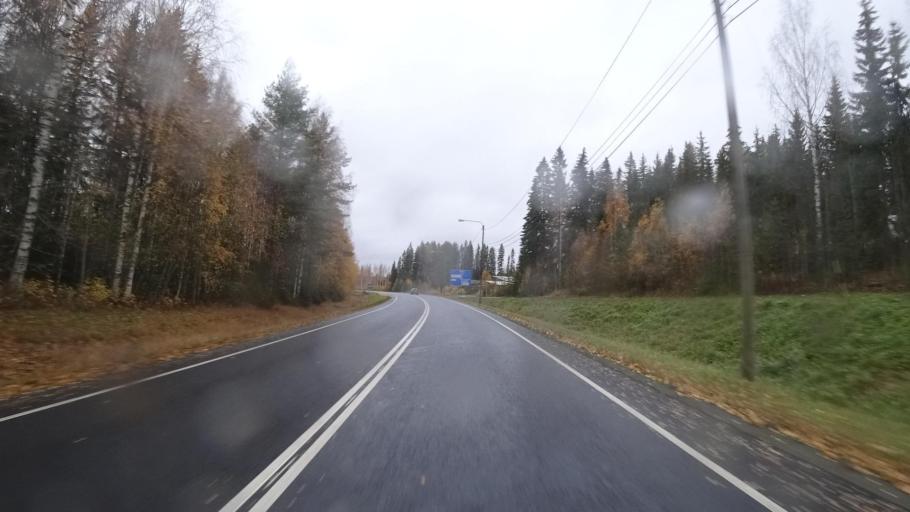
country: FI
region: Northern Savo
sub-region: Kuopio
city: Kuopio
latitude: 62.9837
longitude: 27.7861
